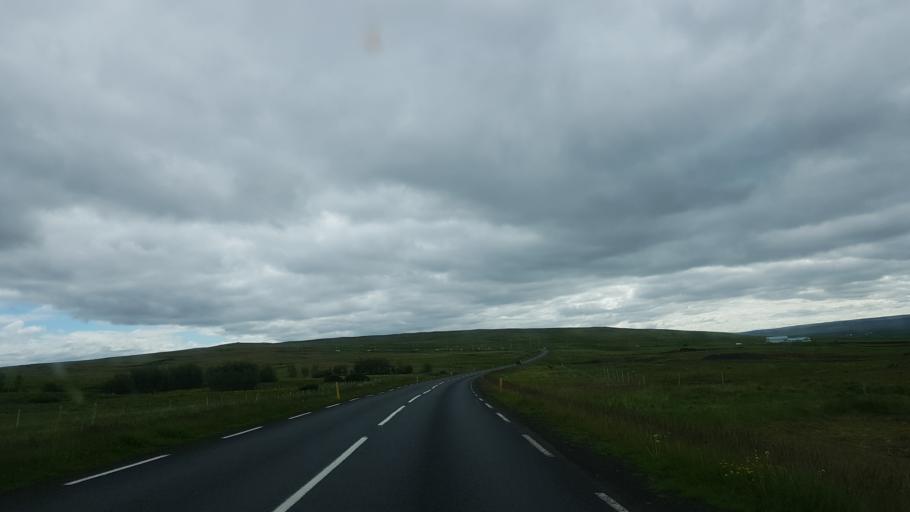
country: IS
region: Northwest
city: Saudarkrokur
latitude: 65.3597
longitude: -20.8905
